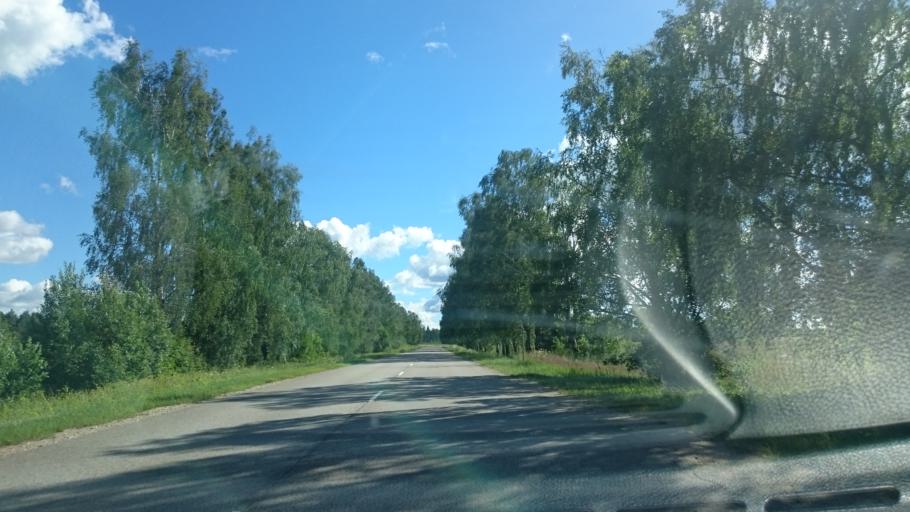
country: LV
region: Kuldigas Rajons
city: Kuldiga
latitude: 56.8986
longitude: 21.8890
